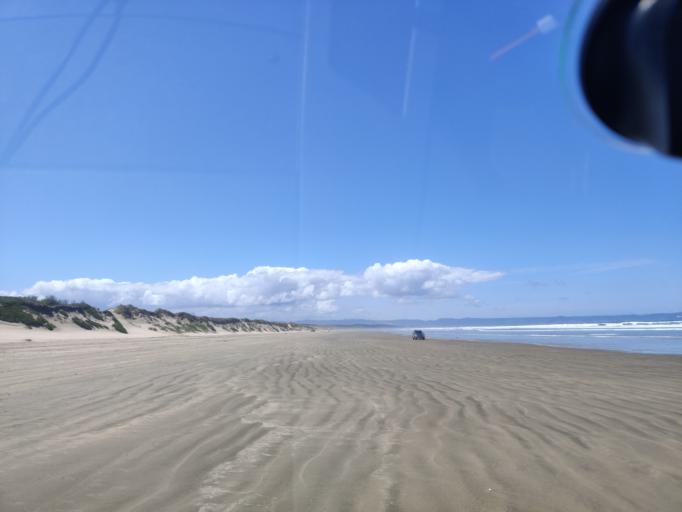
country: NZ
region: Northland
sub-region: Far North District
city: Kaitaia
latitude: -35.0322
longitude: 173.1652
